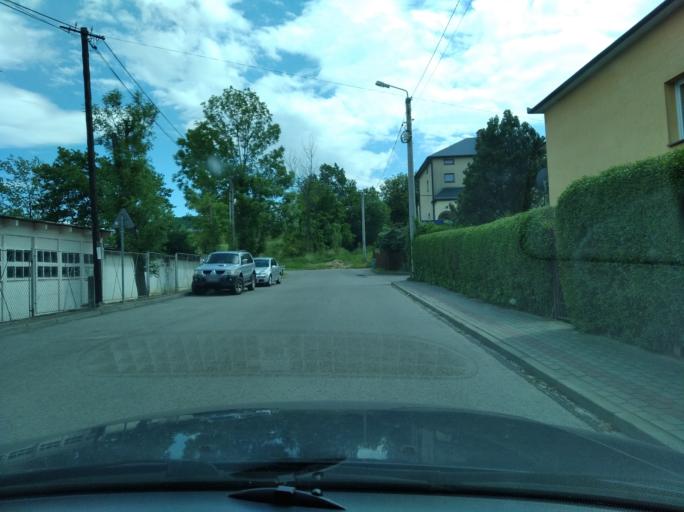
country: PL
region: Subcarpathian Voivodeship
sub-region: Powiat ropczycko-sedziszowski
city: Ropczyce
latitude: 50.0510
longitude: 21.6164
